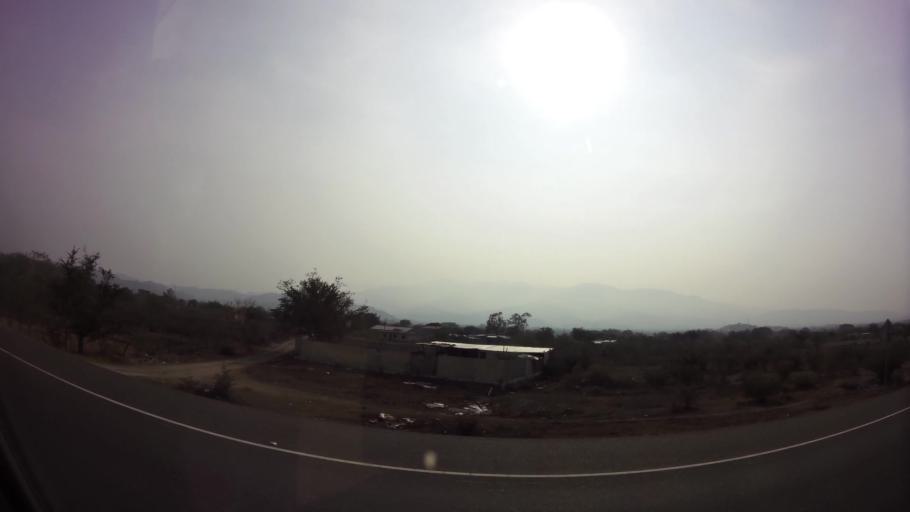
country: HN
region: Comayagua
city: Comayagua
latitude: 14.4454
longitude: -87.6611
